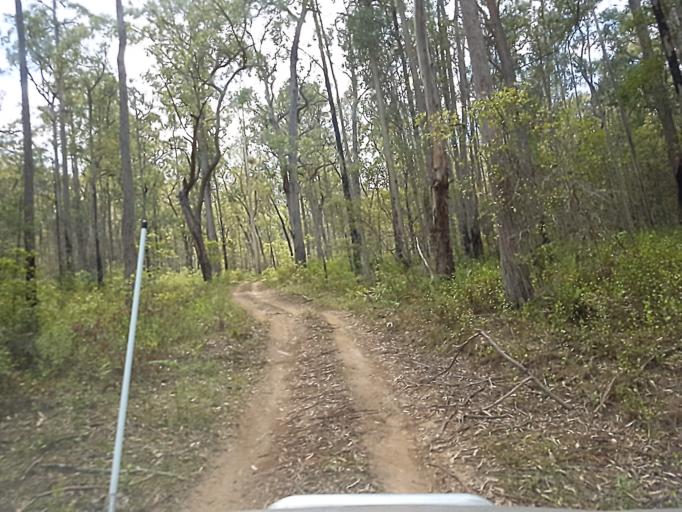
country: AU
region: Victoria
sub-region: East Gippsland
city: Lakes Entrance
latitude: -37.3512
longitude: 148.3558
